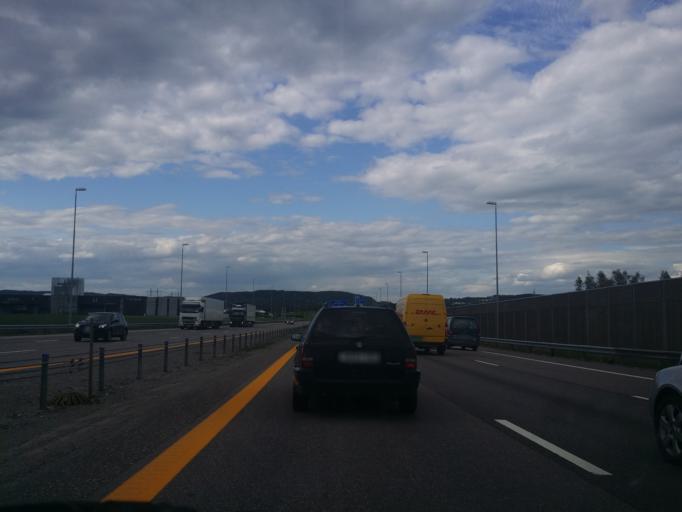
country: NO
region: Akershus
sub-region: Lorenskog
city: Kjenn
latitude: 59.9734
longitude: 10.9909
